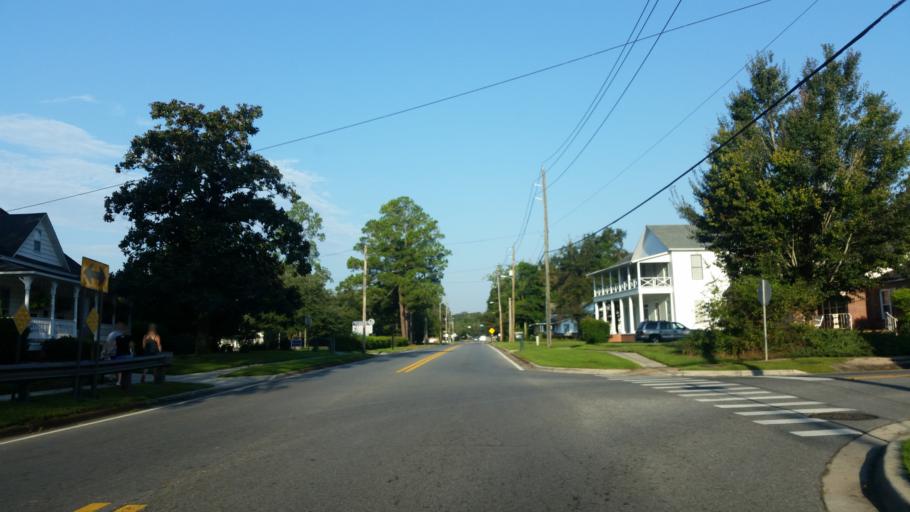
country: US
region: Florida
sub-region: Santa Rosa County
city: Milton
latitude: 30.6248
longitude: -87.0398
